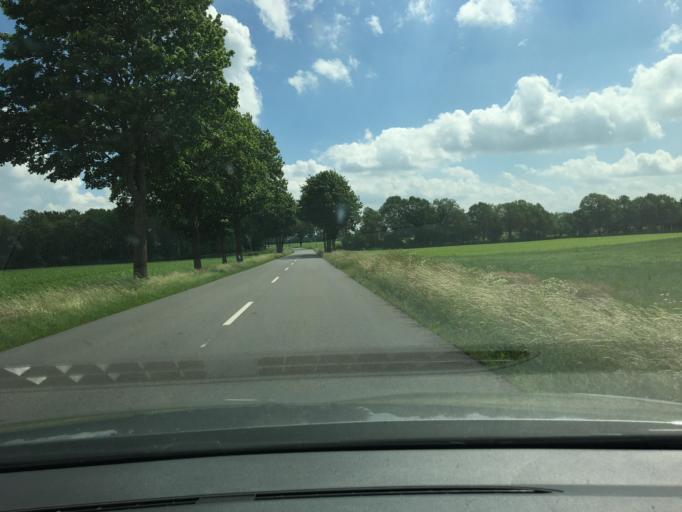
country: DE
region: Lower Saxony
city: Tarmstedt
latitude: 53.2335
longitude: 9.0581
